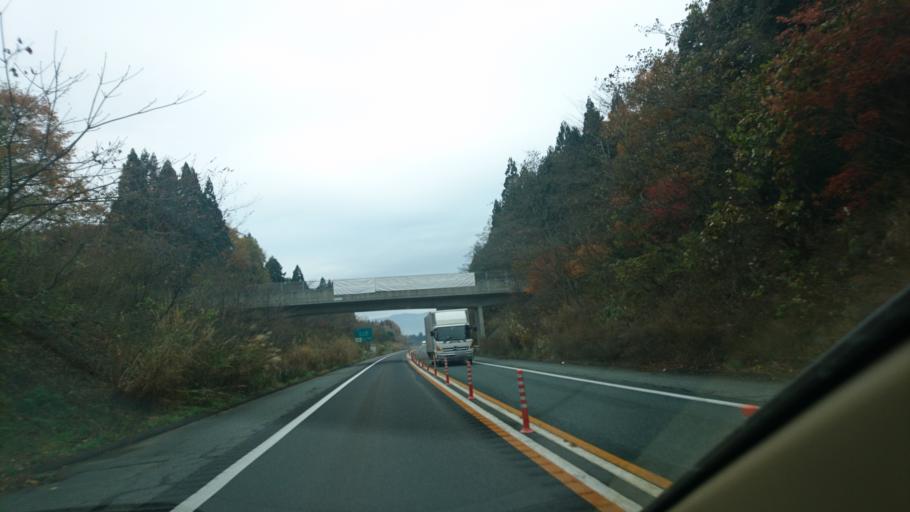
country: JP
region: Iwate
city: Kitakami
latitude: 39.2849
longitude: 140.9964
